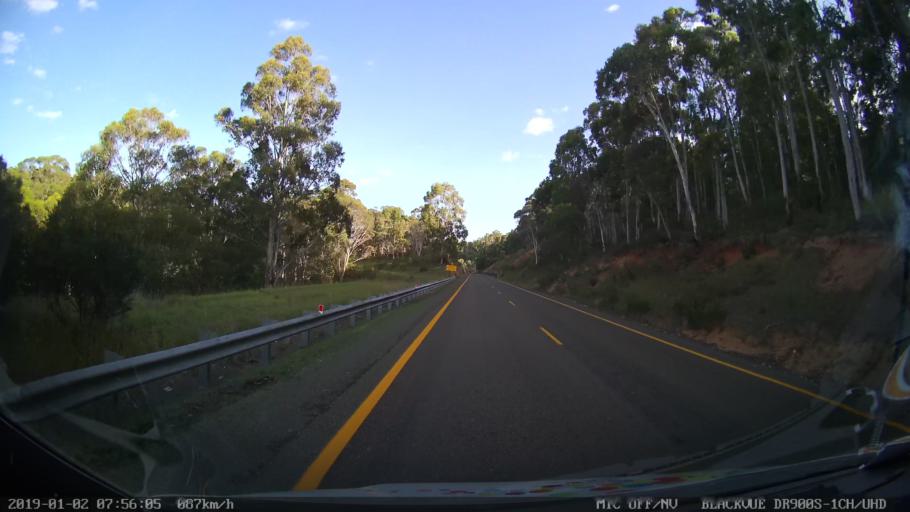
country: AU
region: New South Wales
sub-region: Tumut Shire
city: Tumut
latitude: -35.6751
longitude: 148.4860
